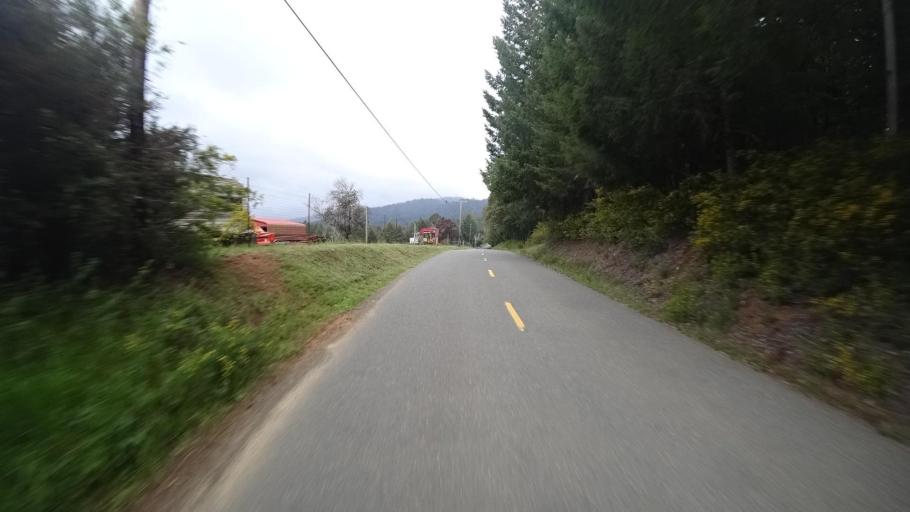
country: US
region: California
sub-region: Humboldt County
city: Redway
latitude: 40.2903
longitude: -123.8126
